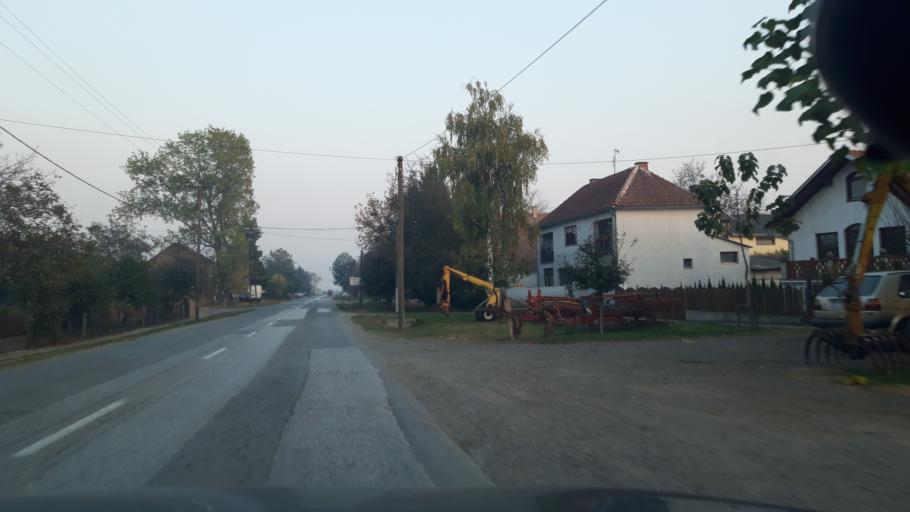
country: RS
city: Putinci
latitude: 45.0016
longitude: 19.9346
